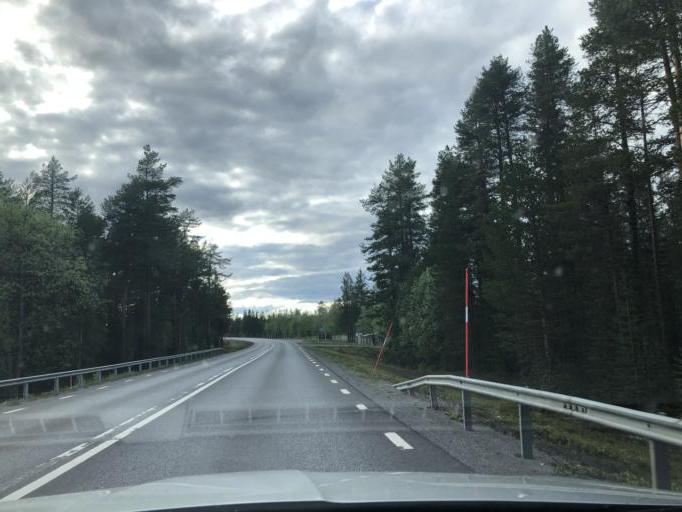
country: SE
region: Norrbotten
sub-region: Arvidsjaurs Kommun
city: Arvidsjaur
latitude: 65.6100
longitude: 19.0769
